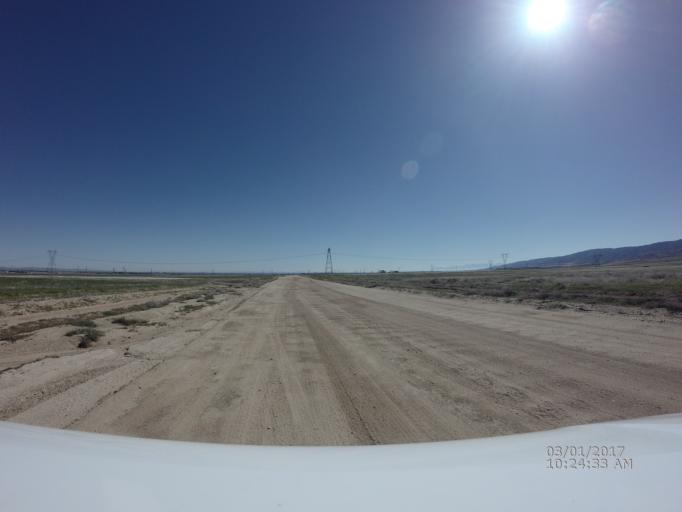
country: US
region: California
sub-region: Los Angeles County
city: Leona Valley
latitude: 34.6892
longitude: -118.3381
